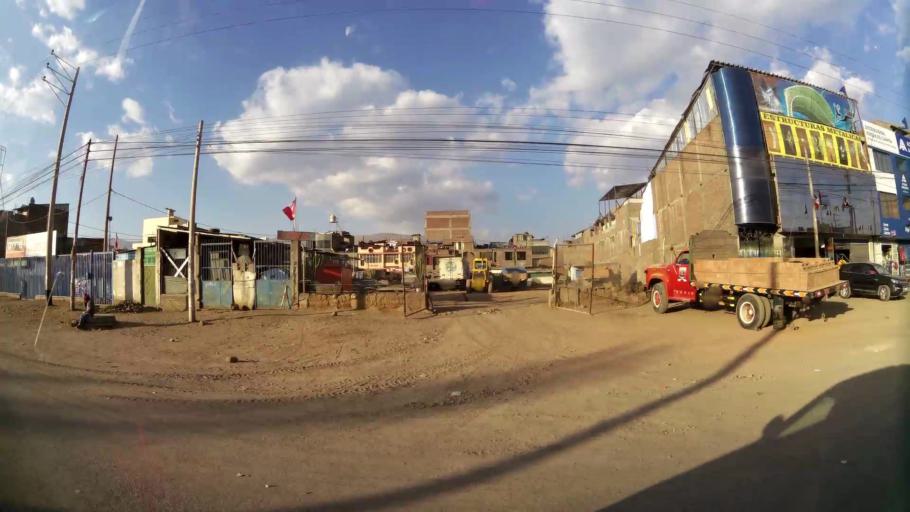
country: PE
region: Junin
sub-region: Provincia de Huancayo
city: Pilcomay
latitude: -12.0382
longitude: -75.2291
